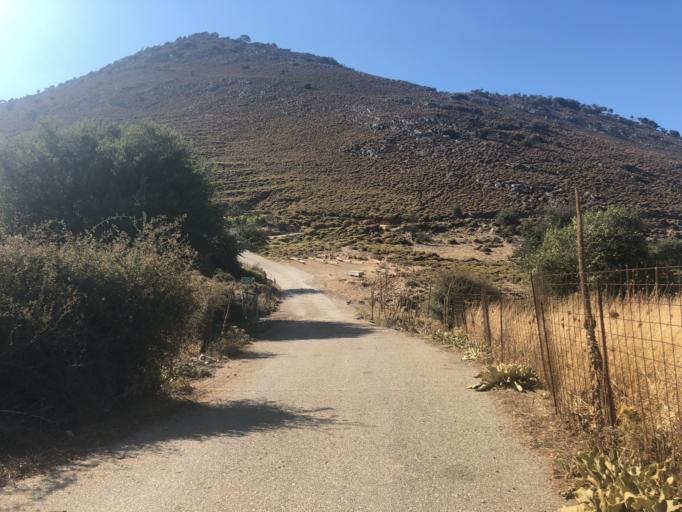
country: GR
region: Crete
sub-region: Nomos Chanias
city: Chora Sfakion
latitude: 35.2524
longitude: 24.1715
